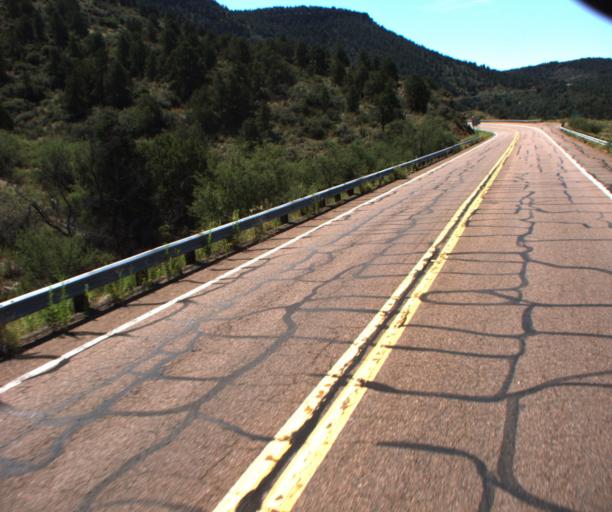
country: US
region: Arizona
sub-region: Navajo County
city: Cibecue
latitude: 33.7892
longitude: -110.5036
